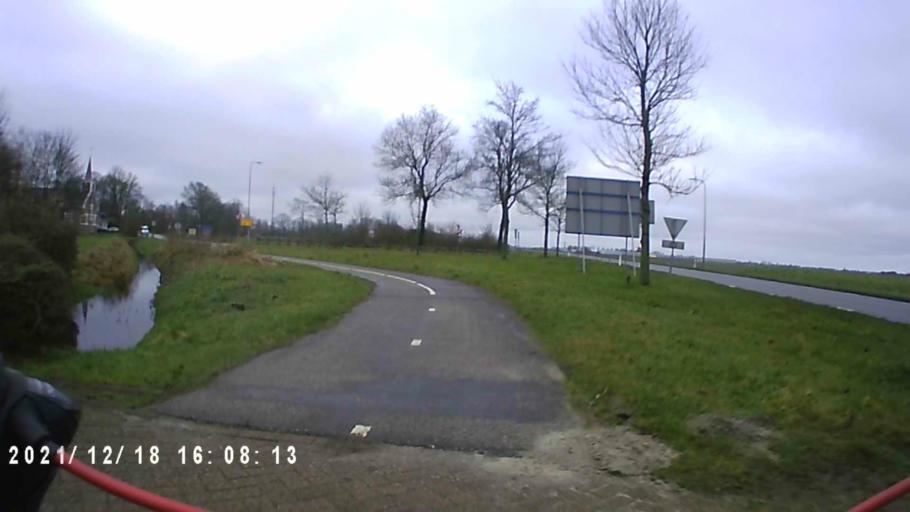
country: NL
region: Friesland
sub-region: Gemeente Dongeradeel
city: Anjum
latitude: 53.3591
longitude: 6.0742
